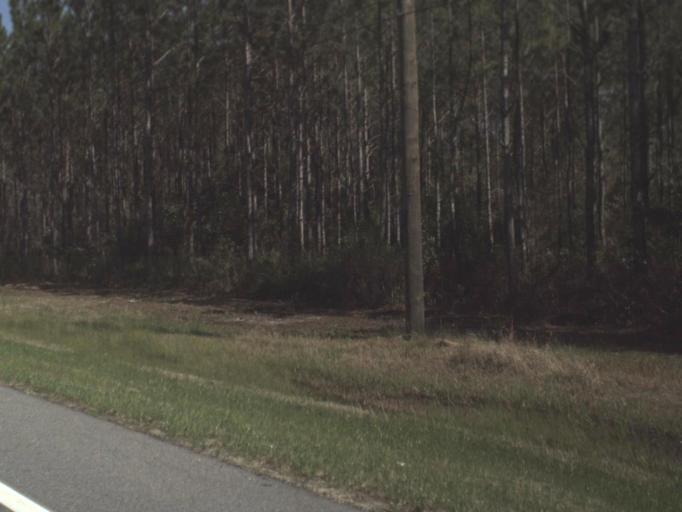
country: US
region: Florida
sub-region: Bay County
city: Panama City Beach
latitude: 30.3257
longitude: -85.7853
